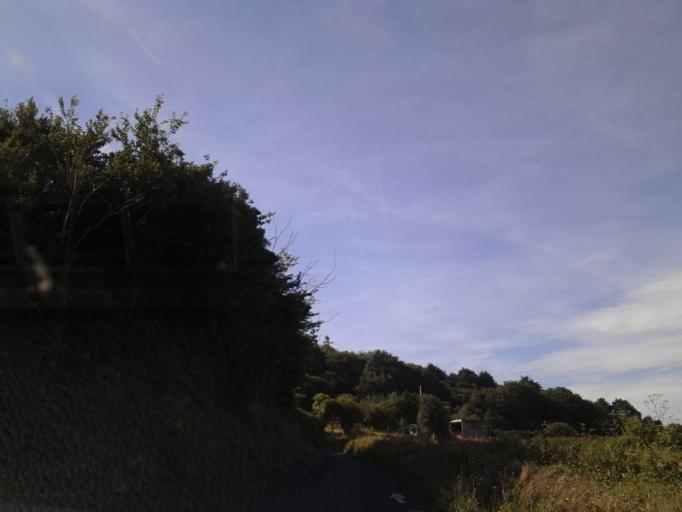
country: FR
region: Lower Normandy
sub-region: Departement de la Manche
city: Tourlaville
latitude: 49.6480
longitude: -1.5683
